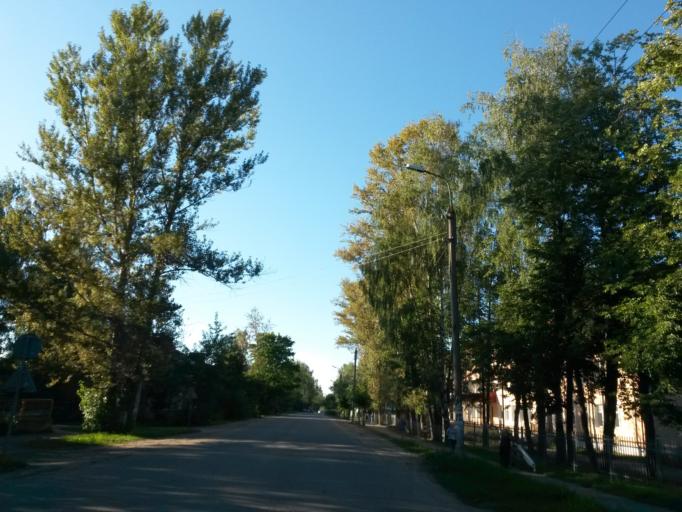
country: RU
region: Jaroslavl
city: Gavrilov-Yam
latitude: 57.3022
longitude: 39.8630
